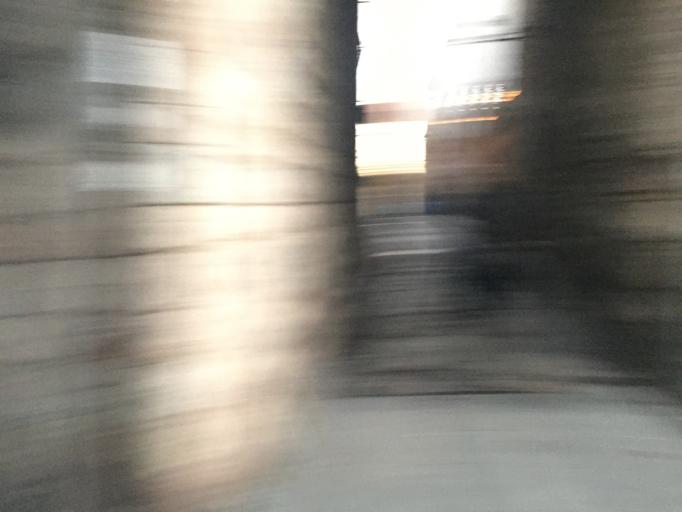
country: IT
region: Umbria
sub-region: Provincia di Perugia
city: Perugia
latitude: 43.1083
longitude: 12.3861
